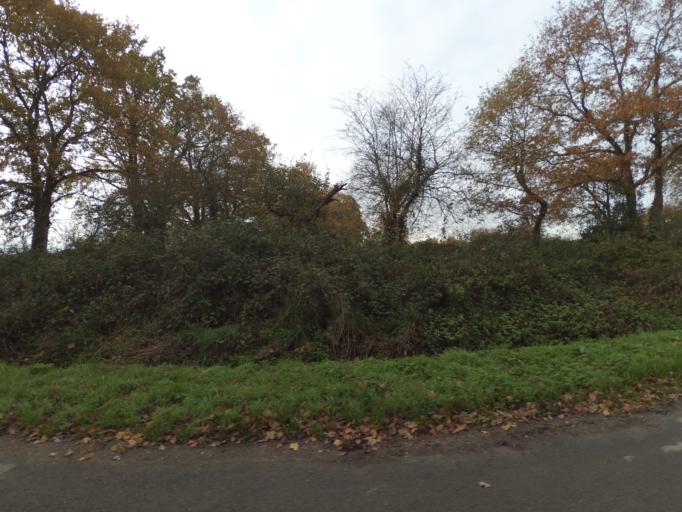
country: FR
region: Pays de la Loire
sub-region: Departement de la Loire-Atlantique
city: La Planche
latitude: 47.0197
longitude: -1.4022
